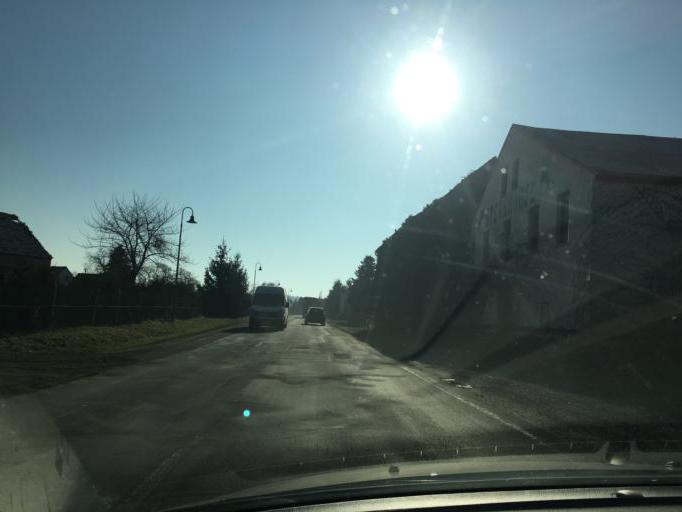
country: DE
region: Saxony
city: Otterwisch
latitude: 51.2134
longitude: 12.6027
